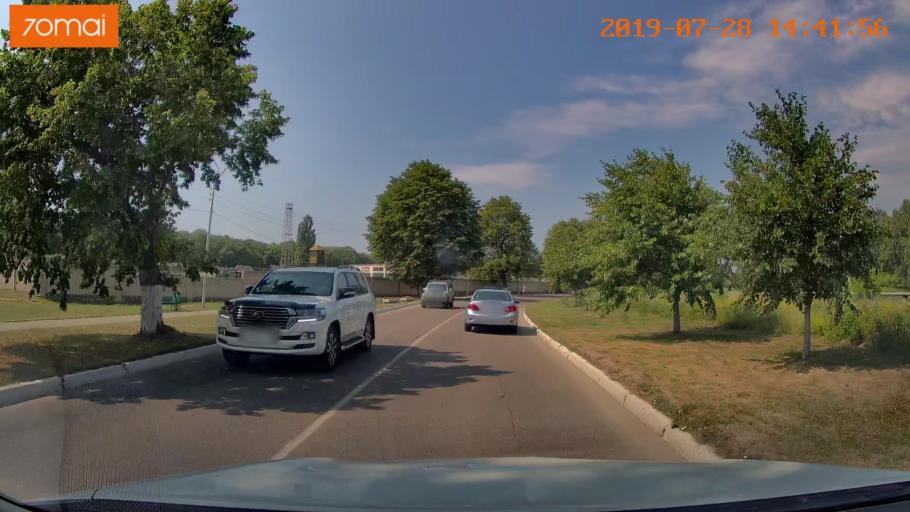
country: RU
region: Kaliningrad
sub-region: Gorod Kaliningrad
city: Yantarnyy
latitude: 54.8573
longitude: 19.9444
